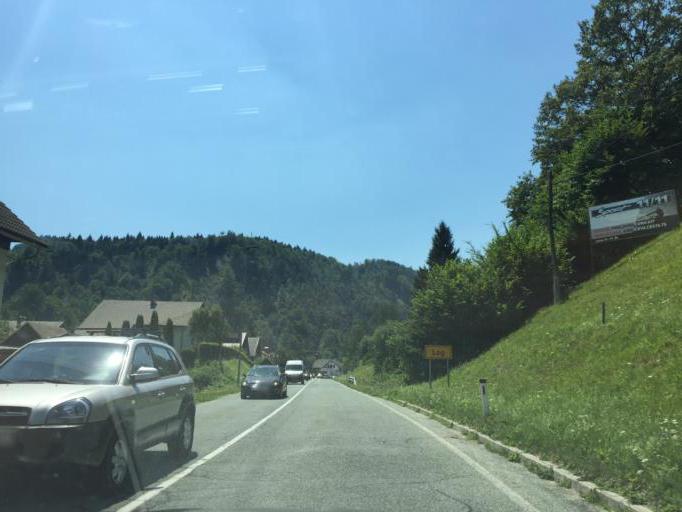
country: SI
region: Gorenja Vas-Poljane
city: Gorenja Vas
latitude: 46.1318
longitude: 14.2285
